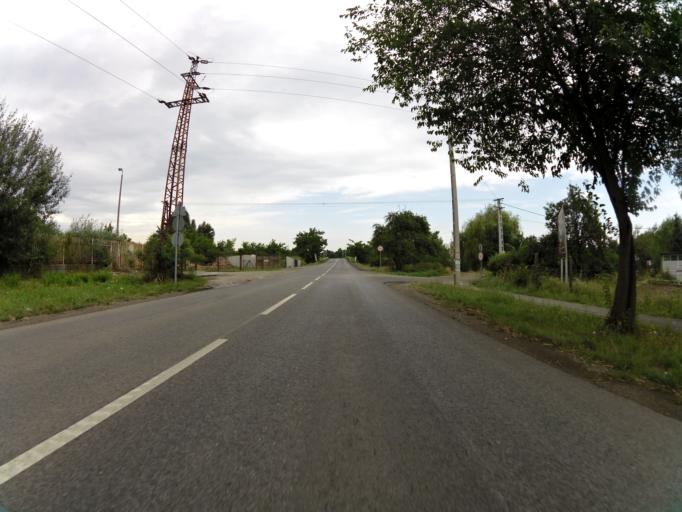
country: HU
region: Csongrad
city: Szeged
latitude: 46.2823
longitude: 20.1436
